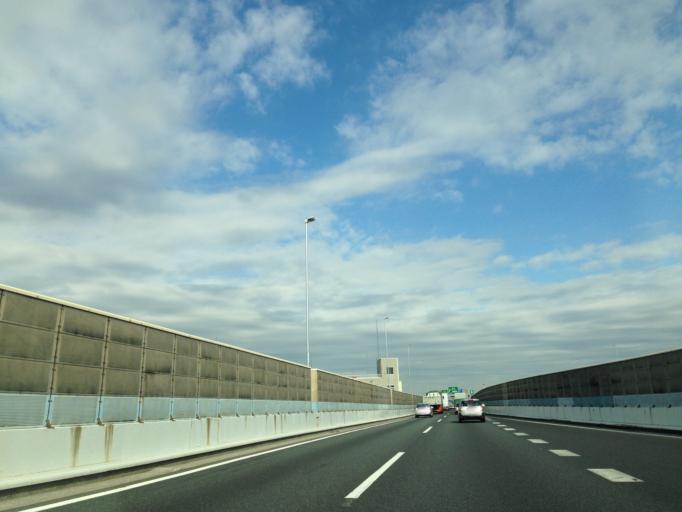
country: JP
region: Saitama
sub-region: Kawaguchi-shi
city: Hatogaya-honcho
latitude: 35.8096
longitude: 139.7587
